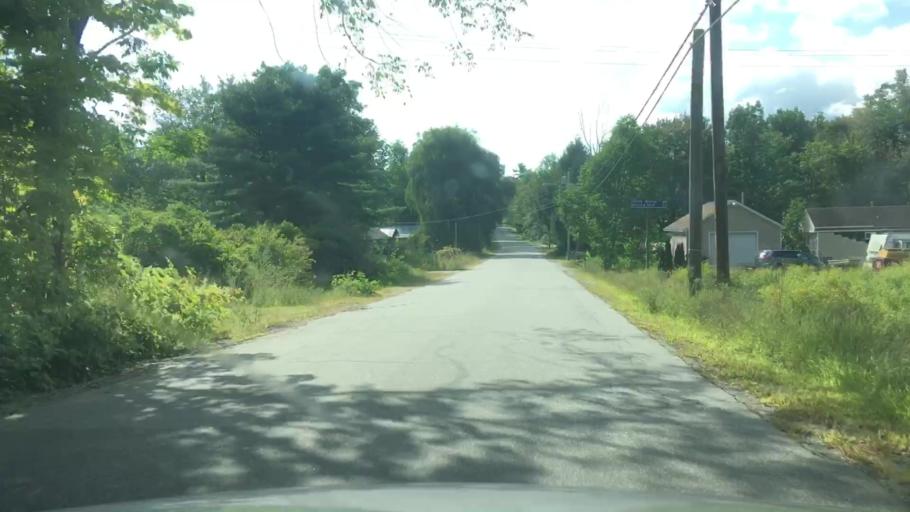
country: US
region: Maine
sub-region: Kennebec County
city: Gardiner
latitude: 44.1745
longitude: -69.8205
